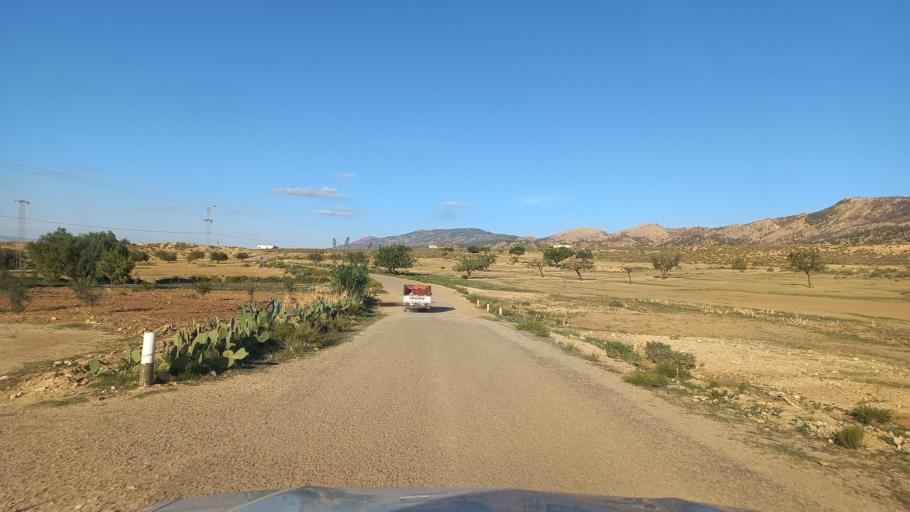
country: TN
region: Al Qasrayn
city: Sbiba
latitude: 35.3513
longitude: 9.1341
